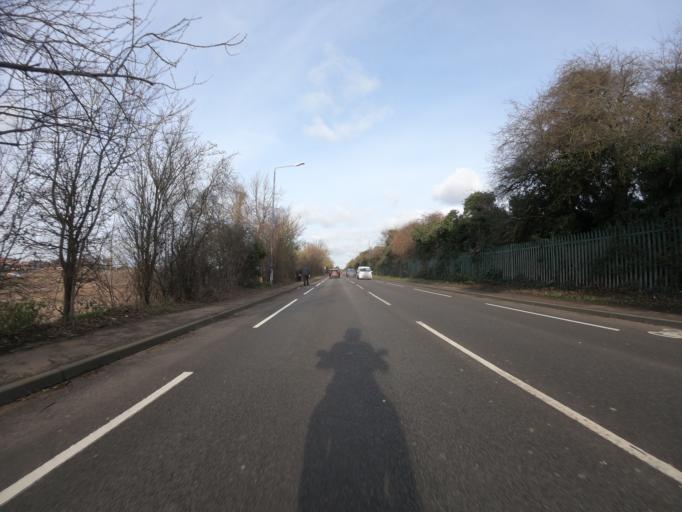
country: GB
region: England
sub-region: Kent
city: Gravesend
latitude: 51.4223
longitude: 0.3616
